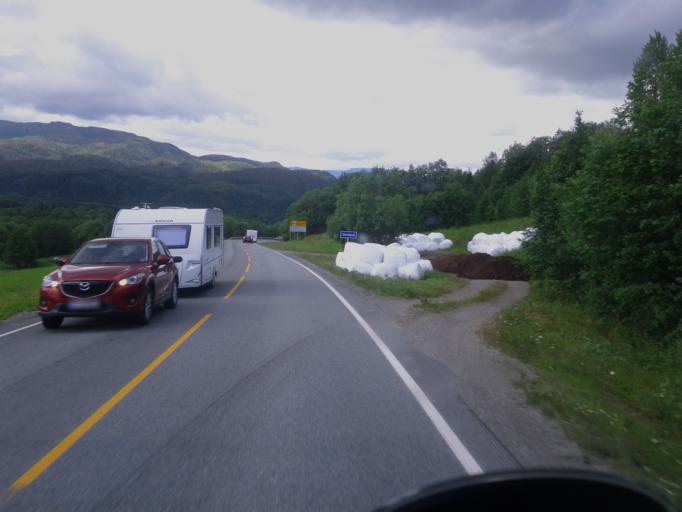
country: NO
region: Nord-Trondelag
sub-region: Grong
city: Grong
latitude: 64.5339
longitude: 12.4110
